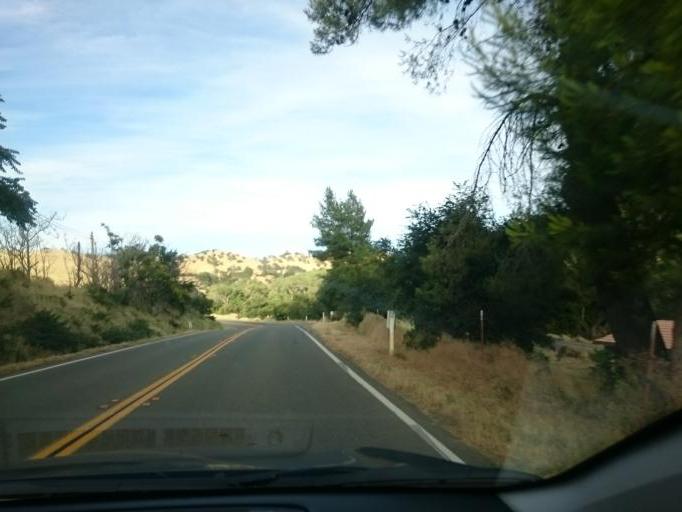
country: US
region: California
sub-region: Yolo County
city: Winters
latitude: 38.5166
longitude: -122.0618
